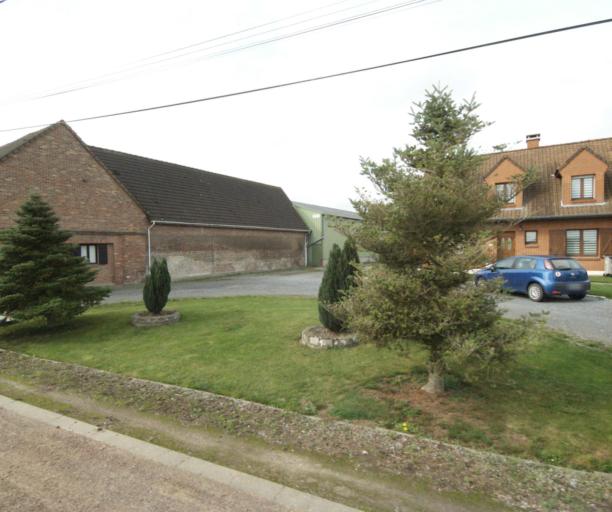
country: FR
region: Nord-Pas-de-Calais
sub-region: Departement du Nord
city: Bois-Grenier
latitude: 50.6368
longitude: 2.8924
